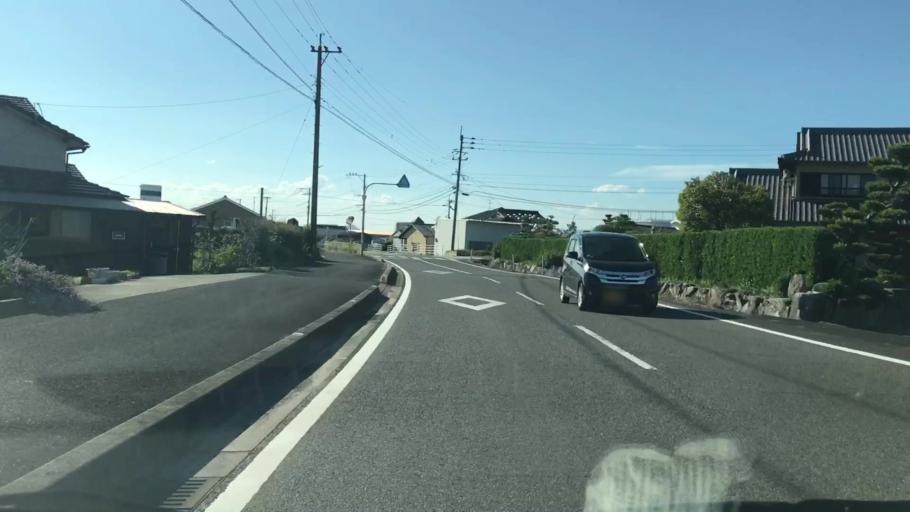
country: JP
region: Saga Prefecture
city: Saga-shi
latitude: 33.1897
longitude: 130.2878
